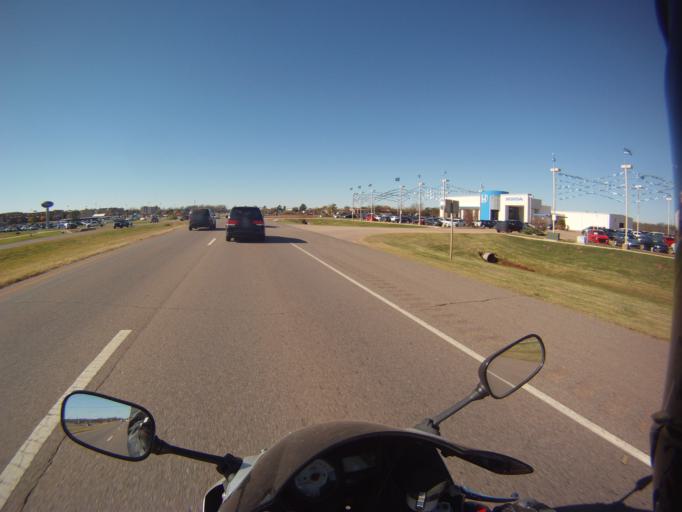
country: US
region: Oklahoma
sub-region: Payne County
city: Stillwater
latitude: 36.1162
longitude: -97.1153
